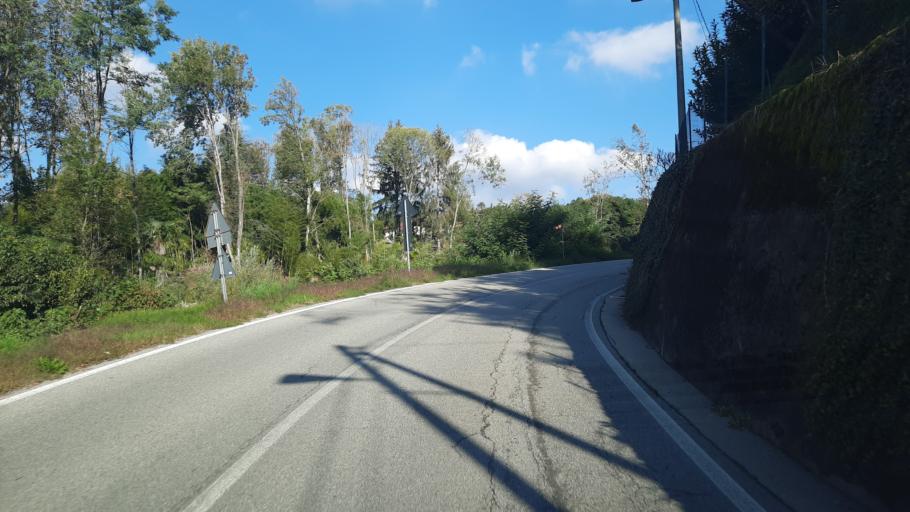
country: IT
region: Piedmont
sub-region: Provincia di Novara
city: Bolzano Novarese
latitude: 45.7600
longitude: 8.4426
